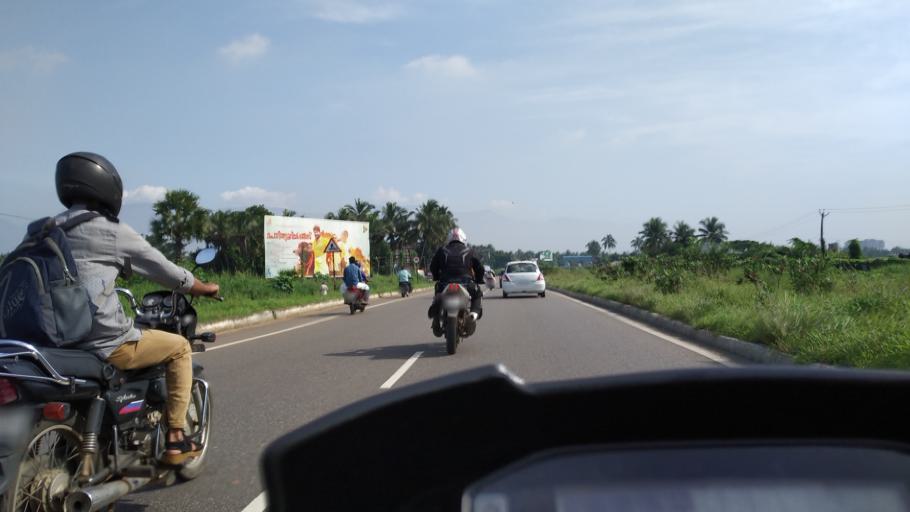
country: IN
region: Kerala
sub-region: Palakkad district
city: Palakkad
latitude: 10.7497
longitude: 76.6618
